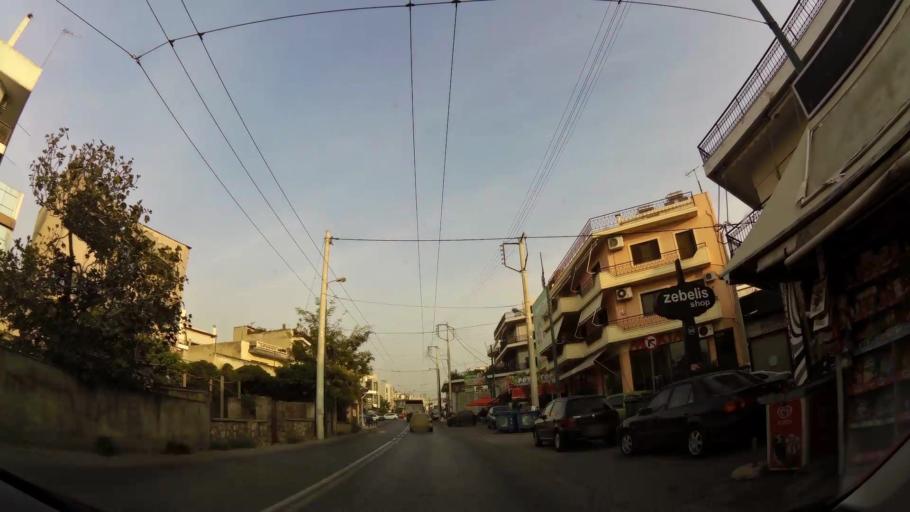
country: GR
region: Attica
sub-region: Nomarchia Athinas
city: Peristeri
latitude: 38.0244
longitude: 23.6834
